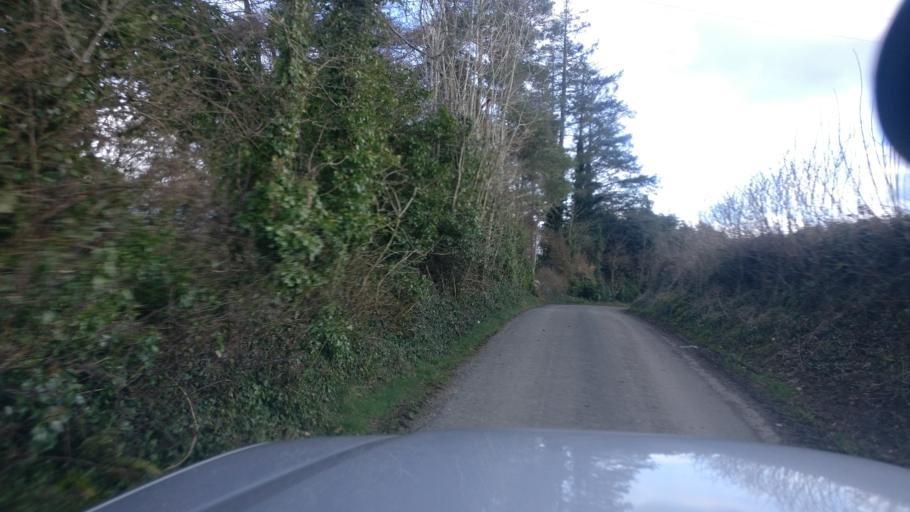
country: IE
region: Connaught
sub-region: County Galway
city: Loughrea
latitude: 53.1815
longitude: -8.4261
